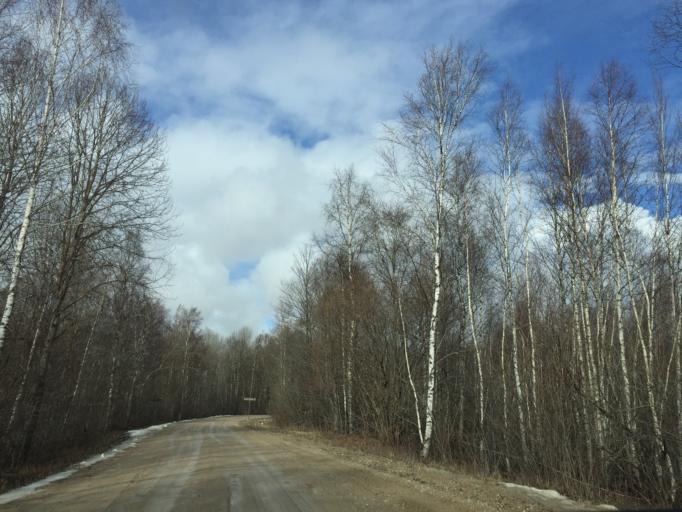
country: EE
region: Laeaene
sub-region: Lihula vald
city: Lihula
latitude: 58.7262
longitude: 23.8299
